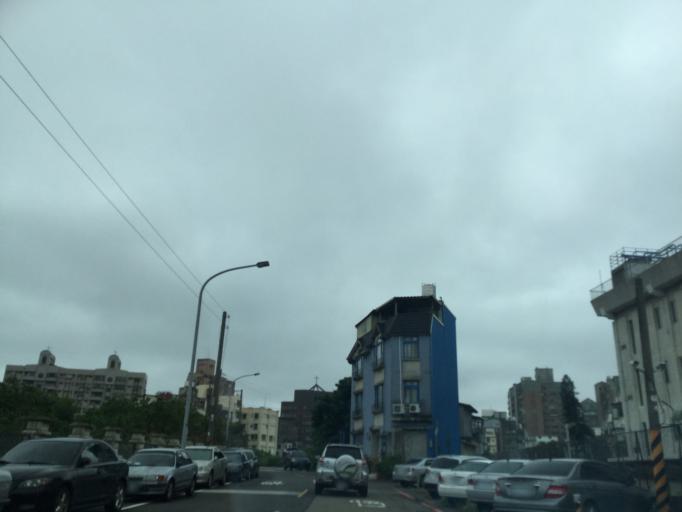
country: TW
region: Taiwan
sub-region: Hsinchu
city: Hsinchu
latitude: 24.7984
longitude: 121.0007
